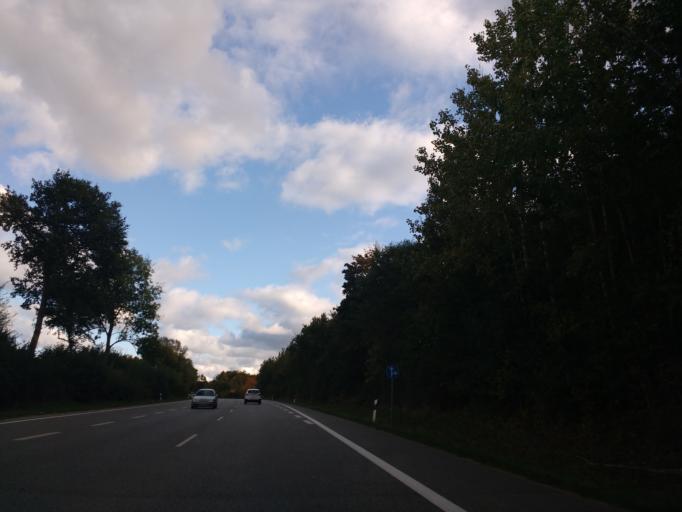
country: DE
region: Schleswig-Holstein
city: Altenkrempe
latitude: 54.1212
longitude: 10.8373
